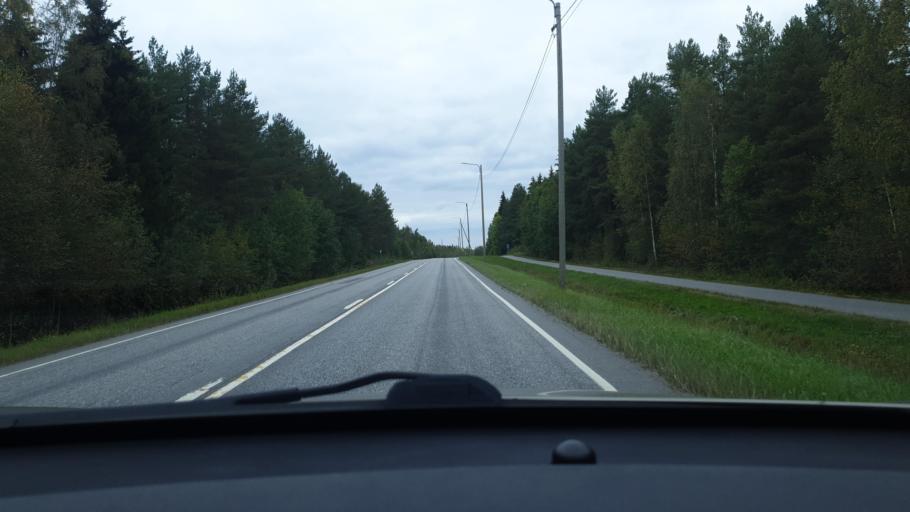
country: FI
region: Ostrobothnia
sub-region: Vaasa
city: Ristinummi
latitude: 63.0570
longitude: 21.7158
